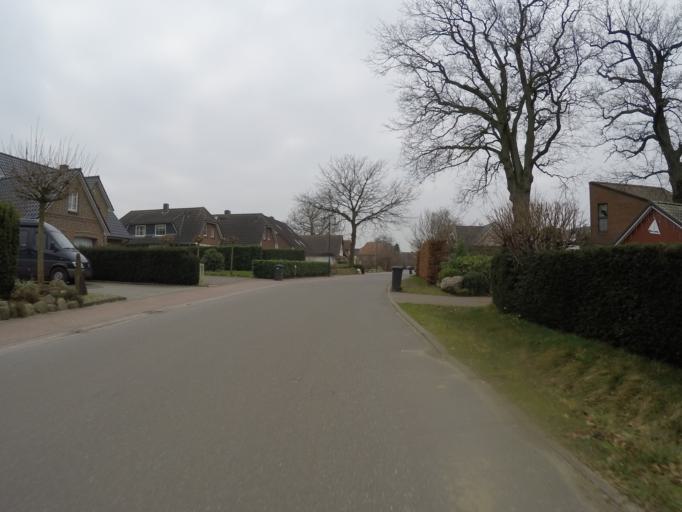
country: DE
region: Schleswig-Holstein
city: Tangstedt
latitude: 53.6856
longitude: 9.8538
